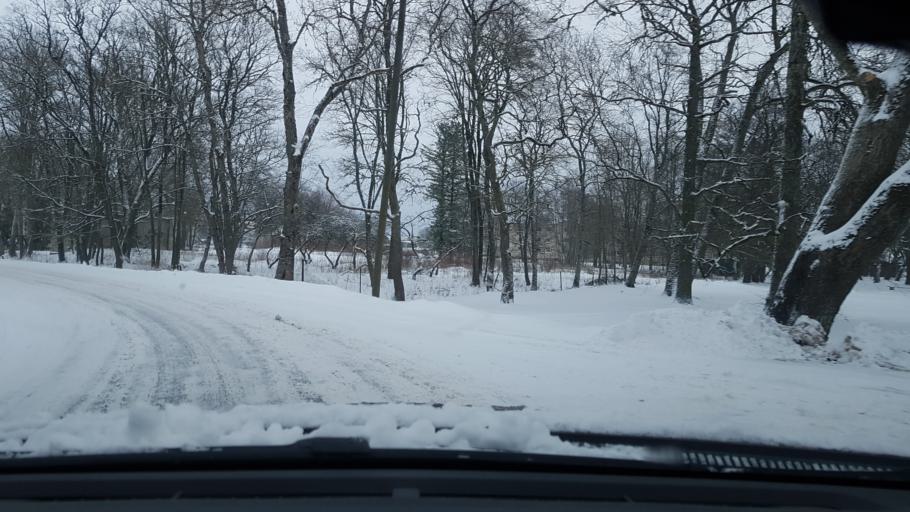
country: EE
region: Harju
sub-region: Kuusalu vald
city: Kuusalu
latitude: 59.4472
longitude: 25.3844
